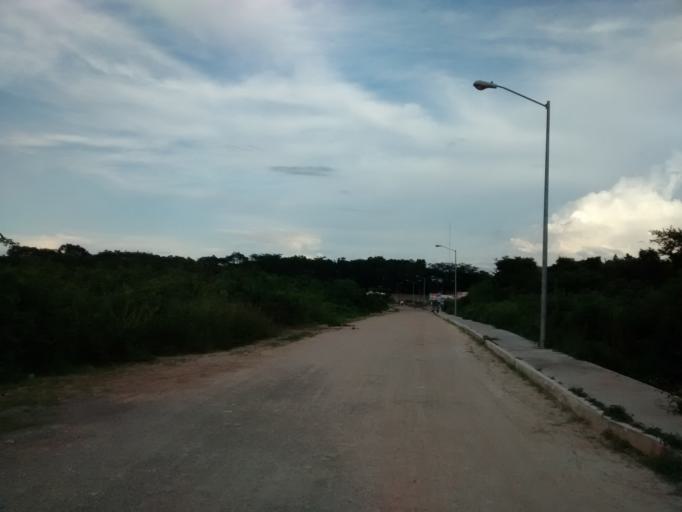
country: MX
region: Yucatan
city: Valladolid
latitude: 20.6878
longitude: -88.1875
